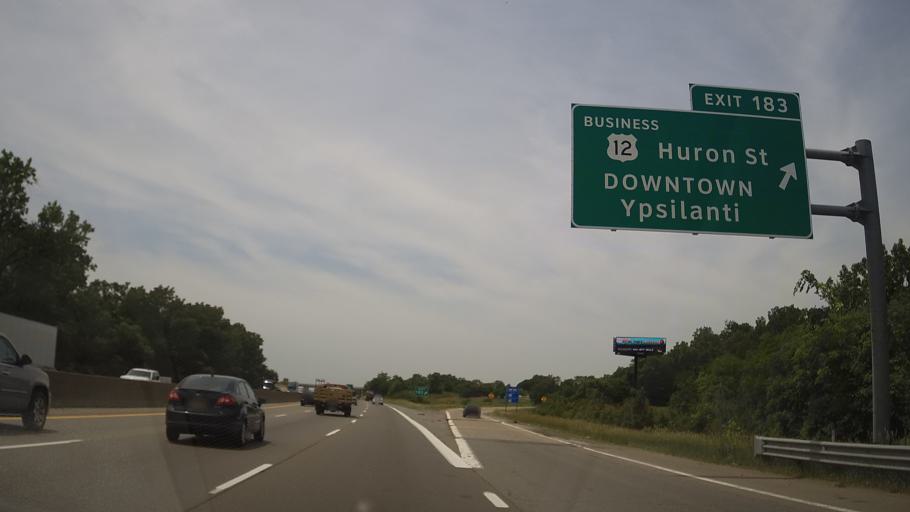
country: US
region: Michigan
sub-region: Washtenaw County
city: Ypsilanti
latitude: 42.2308
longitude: -83.6095
